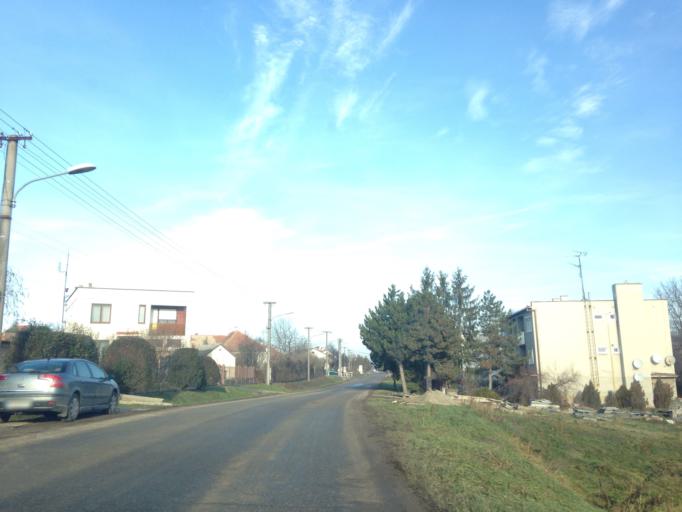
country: SK
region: Nitriansky
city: Svodin
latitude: 47.9632
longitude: 18.4104
